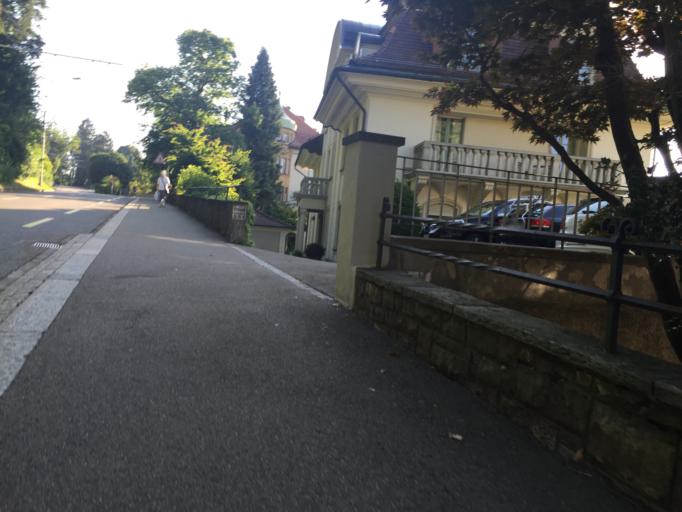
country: CH
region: Saint Gallen
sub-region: Wahlkreis St. Gallen
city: Sankt Gallen
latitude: 47.4302
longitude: 9.3767
